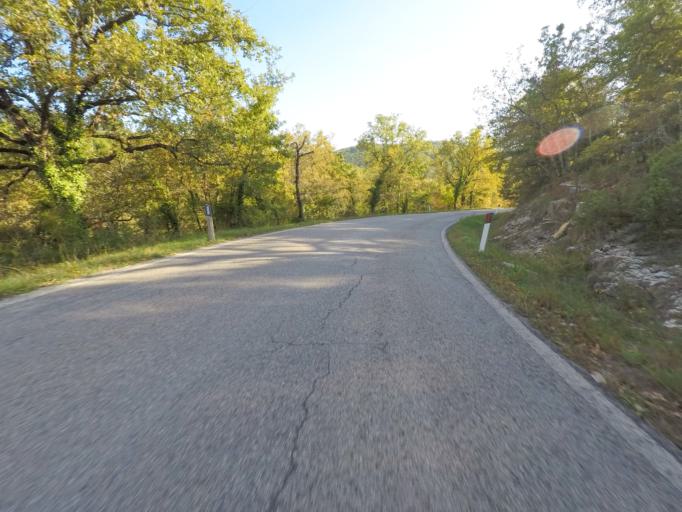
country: IT
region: Tuscany
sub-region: Provincia di Siena
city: Radda in Chianti
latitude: 43.4736
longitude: 11.3743
